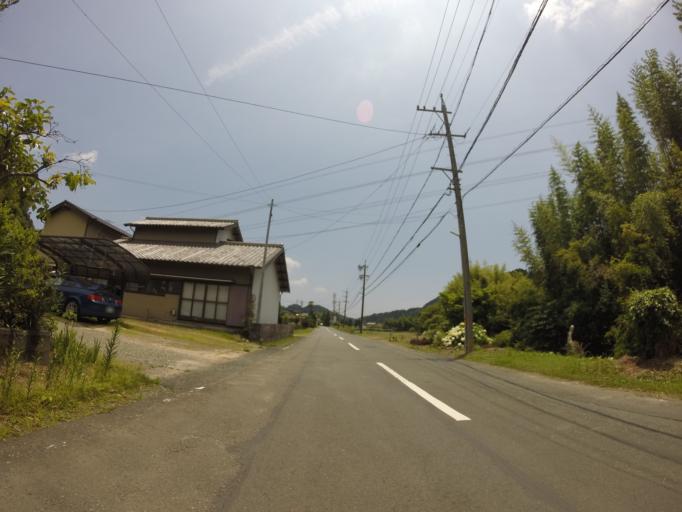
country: JP
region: Shizuoka
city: Kanaya
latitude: 34.8093
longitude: 138.0701
